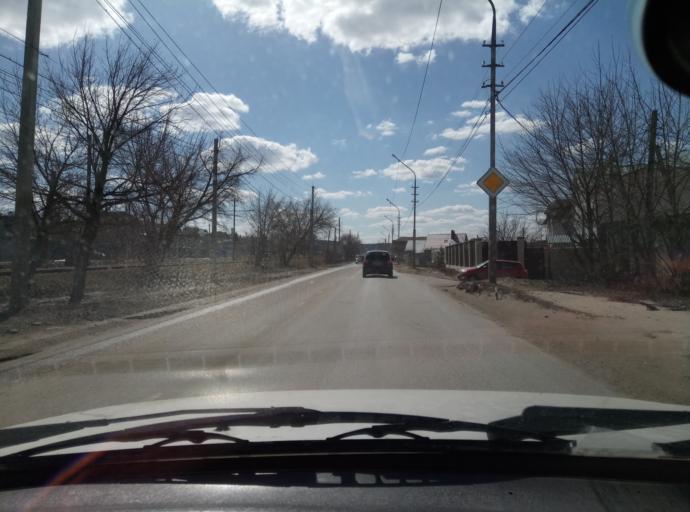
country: RU
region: Saratov
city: Sokolovyy
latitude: 51.5853
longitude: 45.9042
